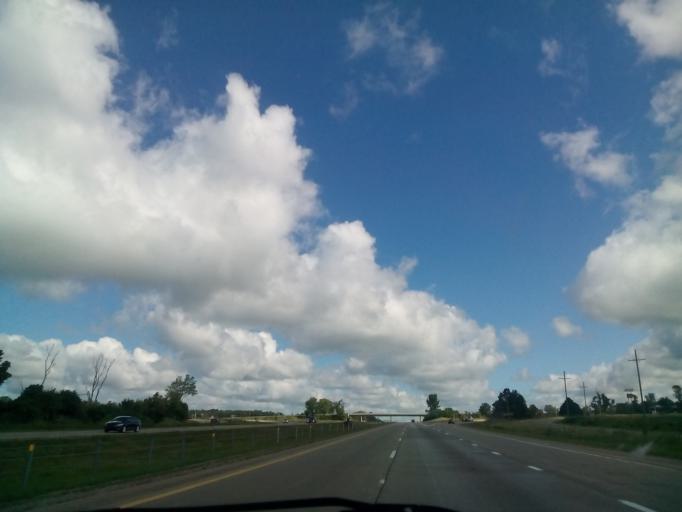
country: US
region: Michigan
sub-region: Genesee County
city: Fenton
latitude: 42.6725
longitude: -83.7595
